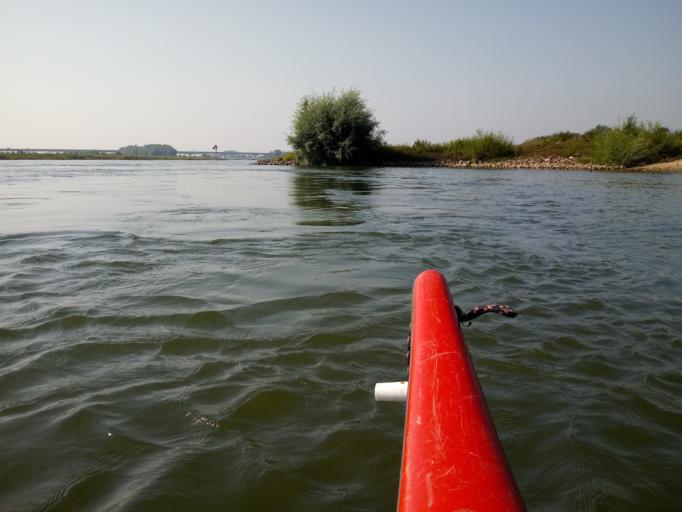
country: NL
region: Gelderland
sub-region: Gemeente Zutphen
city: Zutphen
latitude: 52.1288
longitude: 6.1887
